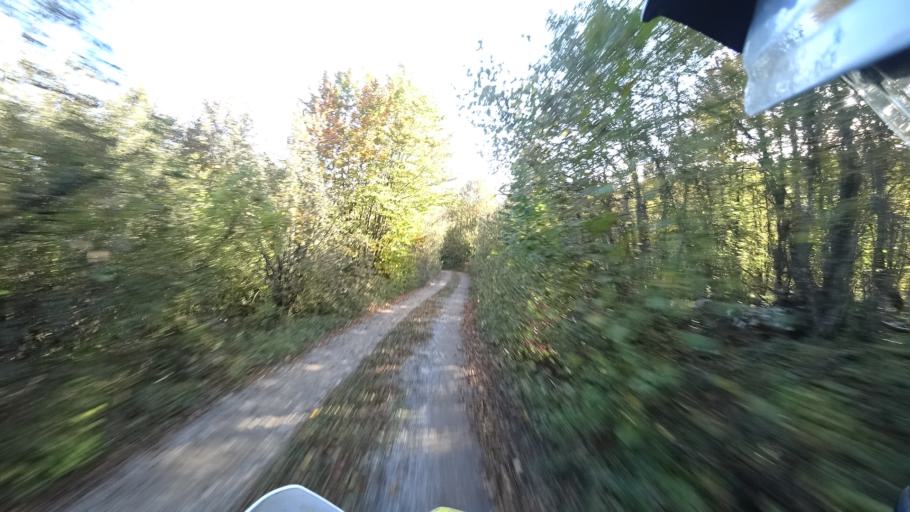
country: HR
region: Karlovacka
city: Plaski
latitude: 45.0310
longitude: 15.3904
